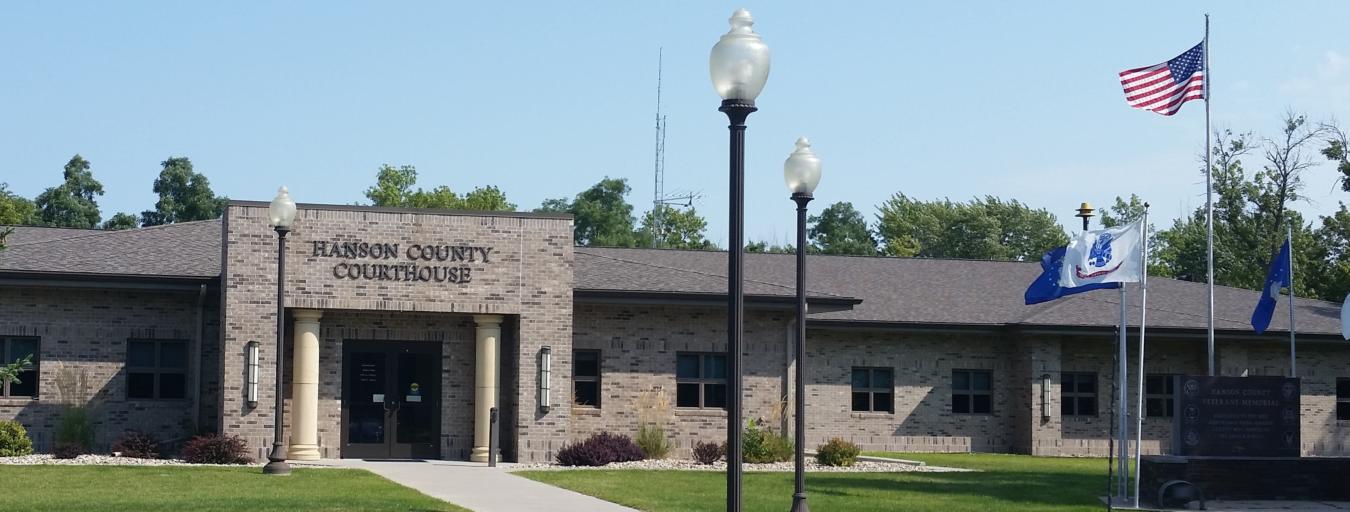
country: US
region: South Dakota
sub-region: Hanson County
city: Alexandria
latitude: 43.6545
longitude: -97.7781
